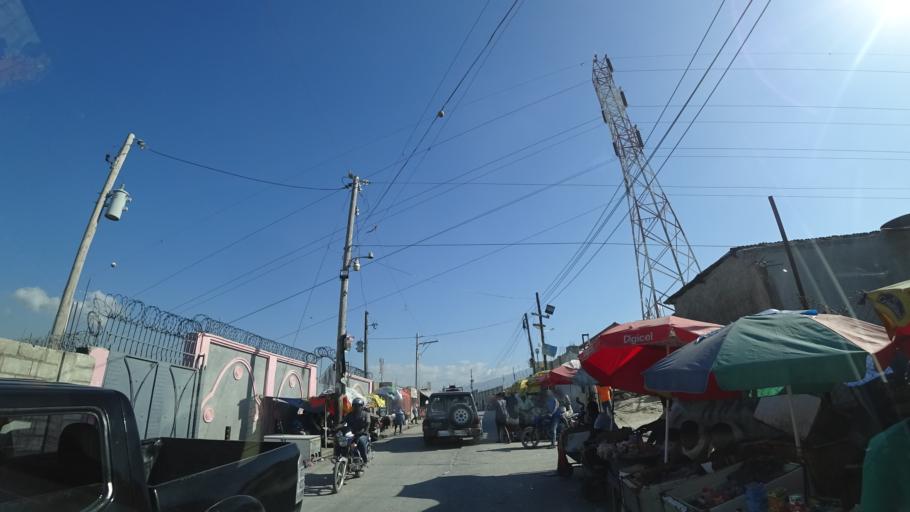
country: HT
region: Ouest
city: Delmas 73
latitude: 18.5626
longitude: -72.2871
